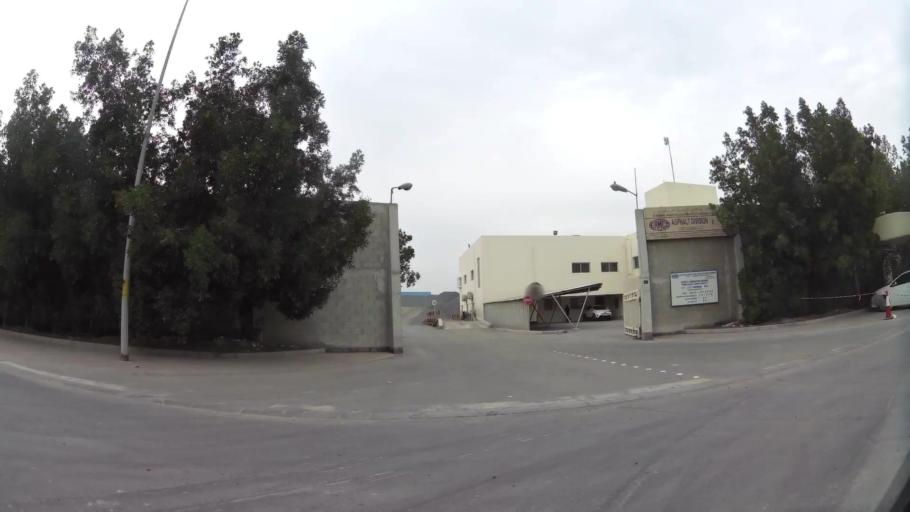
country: BH
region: Northern
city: Sitrah
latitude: 26.1270
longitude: 50.6050
